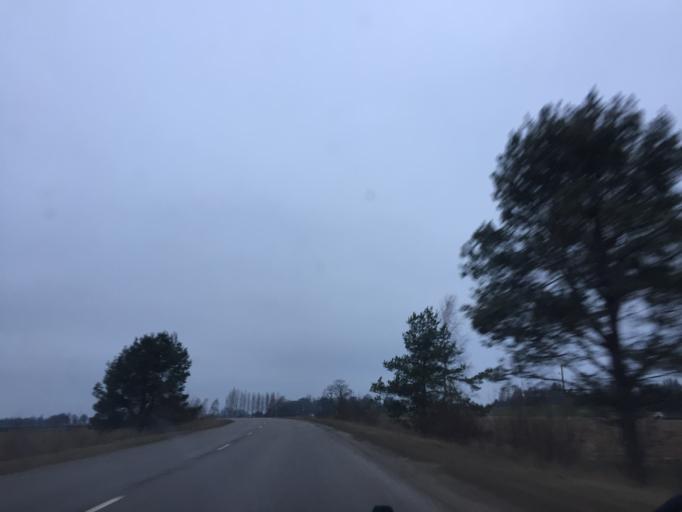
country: LV
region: Raunas
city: Rauna
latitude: 57.3345
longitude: 25.5196
